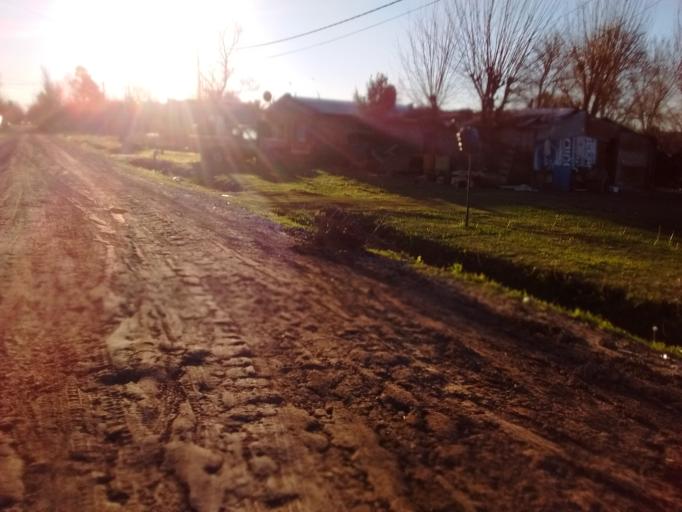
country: AR
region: Santa Fe
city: Funes
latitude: -32.9109
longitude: -60.8548
